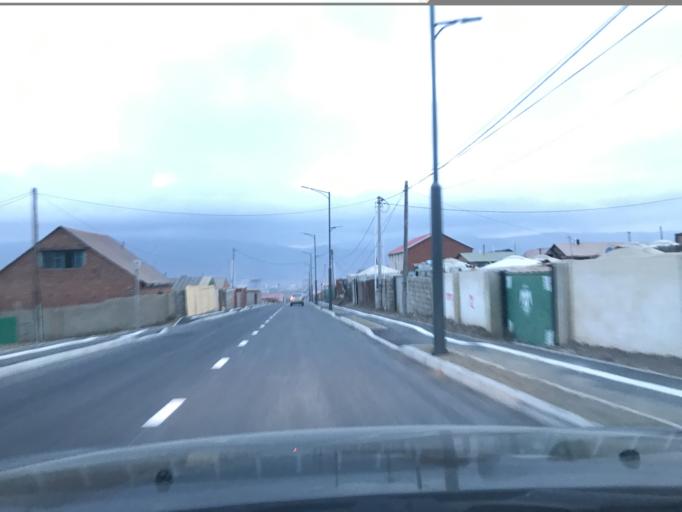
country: MN
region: Ulaanbaatar
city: Ulaanbaatar
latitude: 47.9303
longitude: 106.9739
